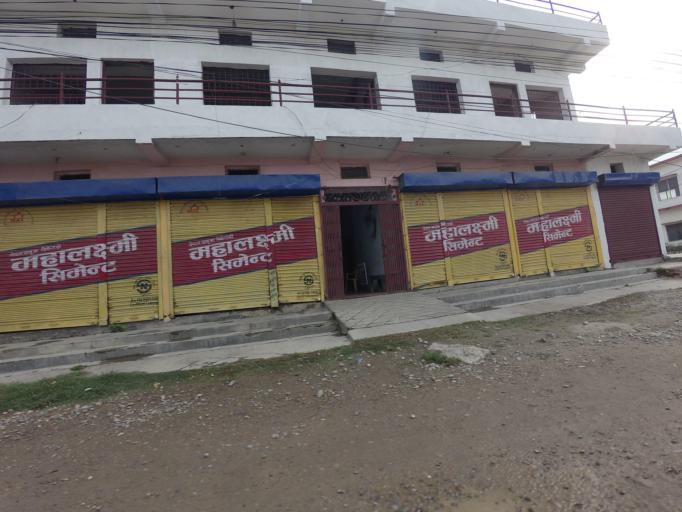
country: NP
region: Western Region
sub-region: Lumbini Zone
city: Bhairahawa
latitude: 27.5205
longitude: 83.4421
